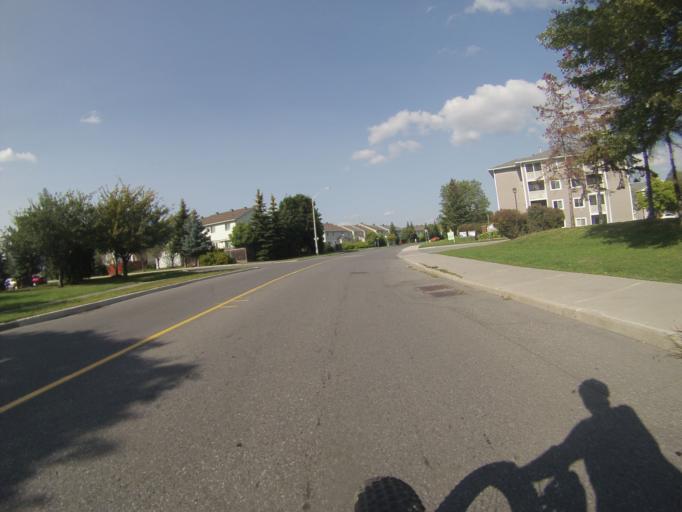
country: CA
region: Ontario
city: Ottawa
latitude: 45.3637
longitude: -75.6346
